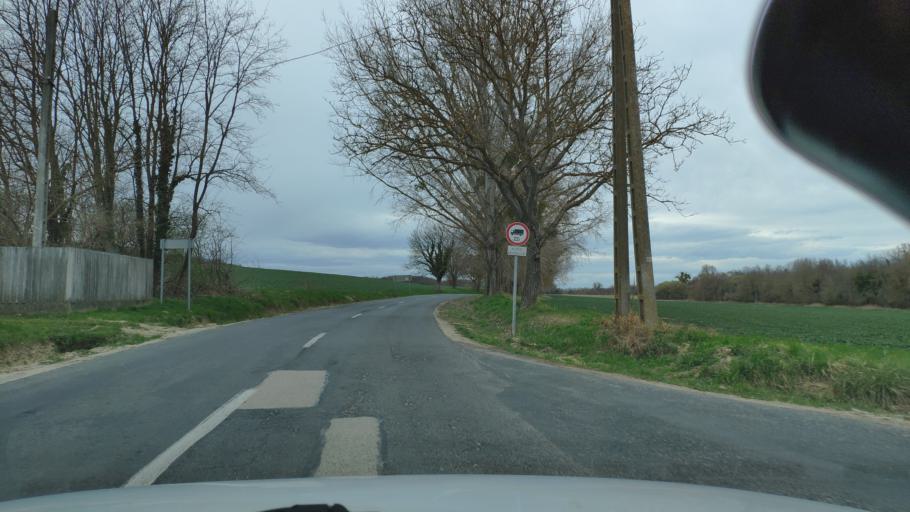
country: HU
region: Zala
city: Sarmellek
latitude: 46.6574
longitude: 17.1143
